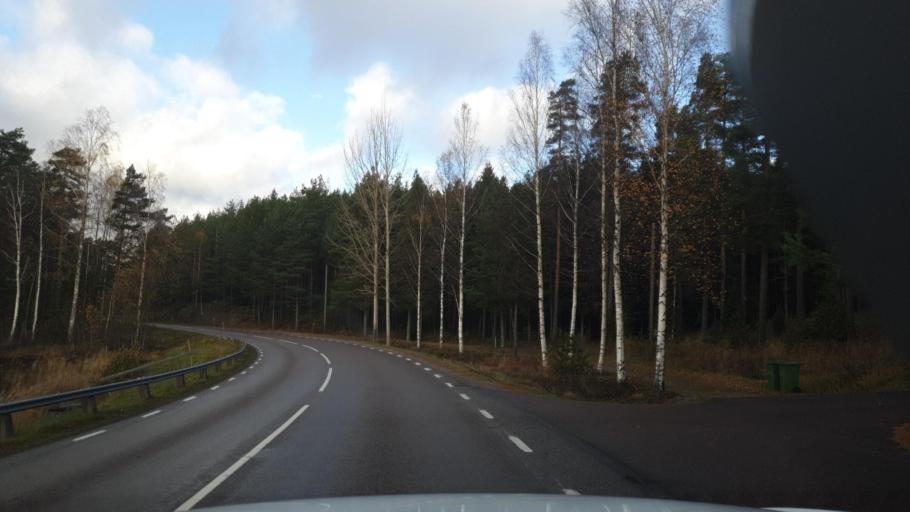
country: SE
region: Vaermland
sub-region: Grums Kommun
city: Slottsbron
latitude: 59.4514
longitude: 12.8965
